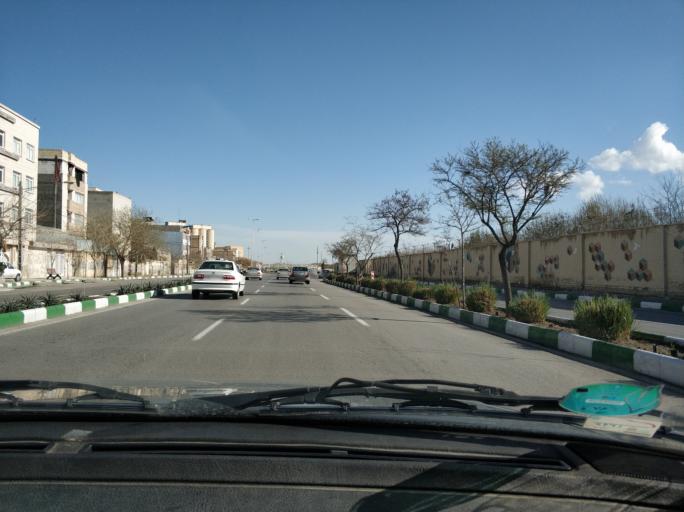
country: IR
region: Razavi Khorasan
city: Mashhad
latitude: 36.3087
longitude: 59.6253
